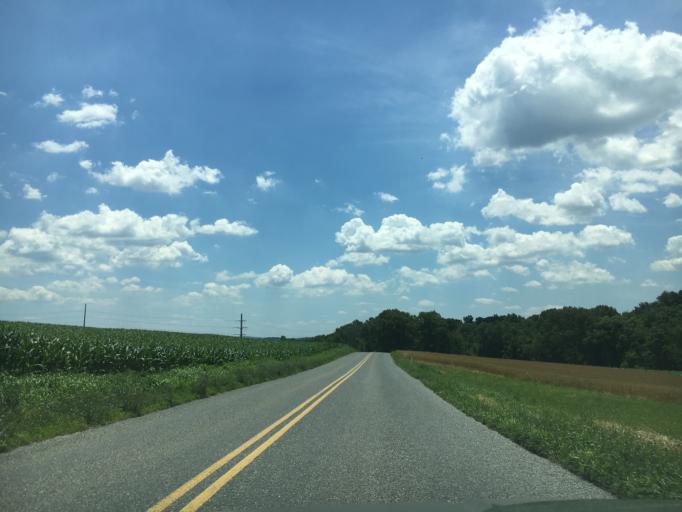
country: US
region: Pennsylvania
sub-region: Lehigh County
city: Schnecksville
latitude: 40.6719
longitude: -75.5792
